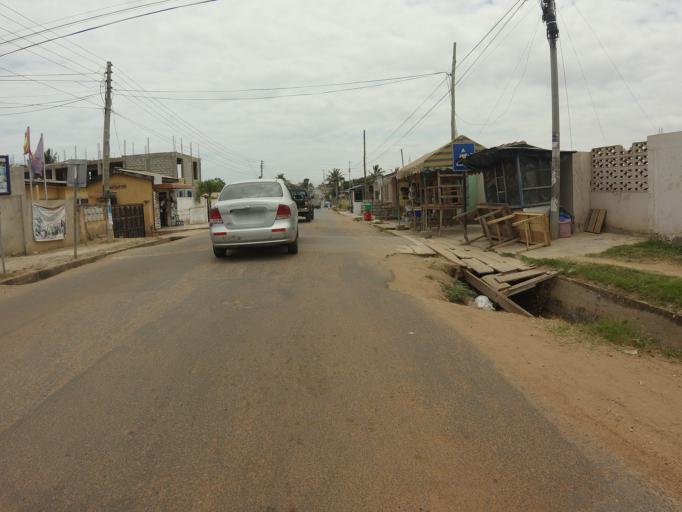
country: GH
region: Greater Accra
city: Nungua
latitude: 5.6072
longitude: -0.0955
